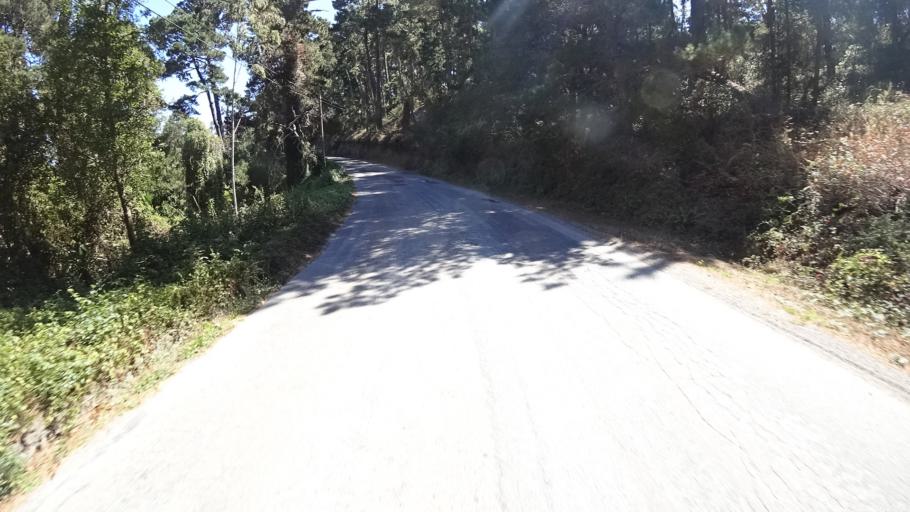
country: US
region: California
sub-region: Monterey County
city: Carmel-by-the-Sea
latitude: 36.5706
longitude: -121.9037
